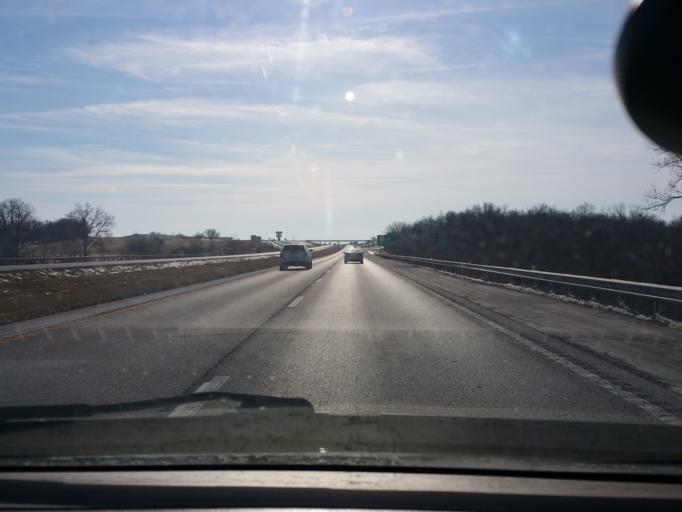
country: US
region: Missouri
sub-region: Clinton County
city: Cameron
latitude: 39.7392
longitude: -94.2205
